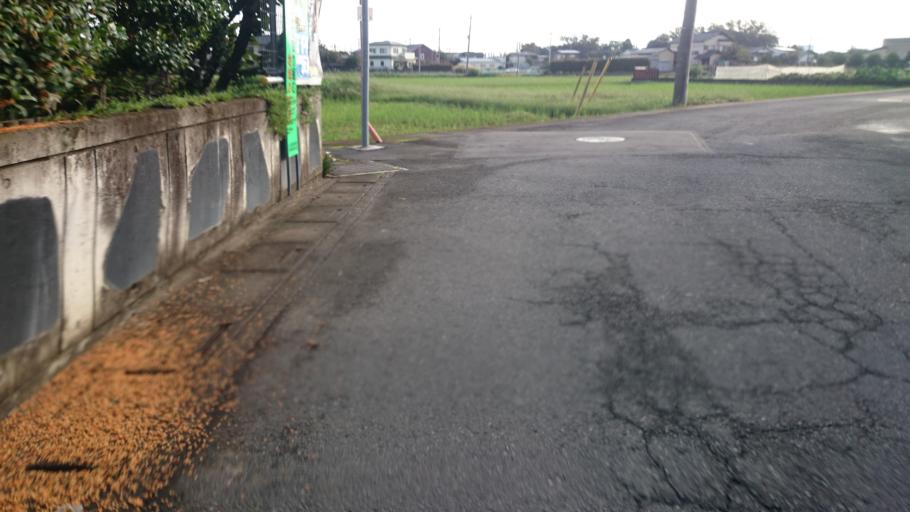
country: JP
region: Saitama
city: Kamifukuoka
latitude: 35.9057
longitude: 139.5691
